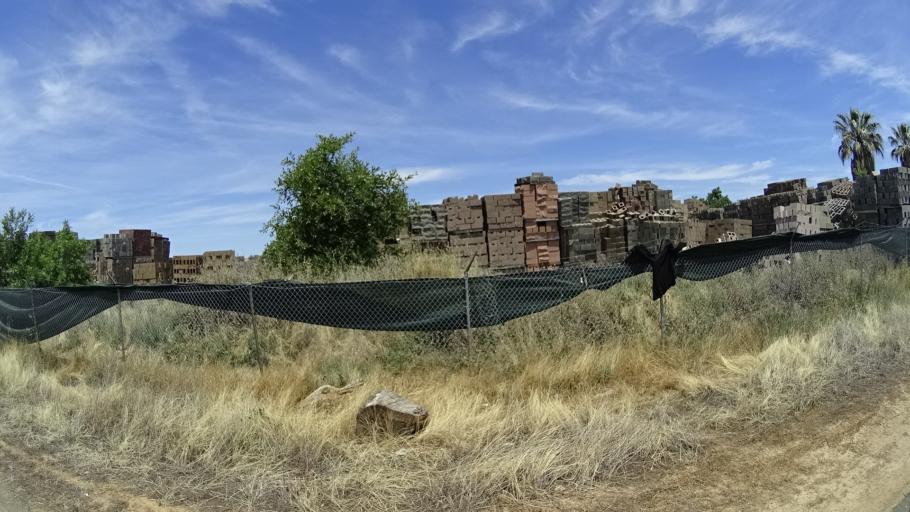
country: US
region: California
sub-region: Sacramento County
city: Florin
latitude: 38.5324
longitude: -121.4028
